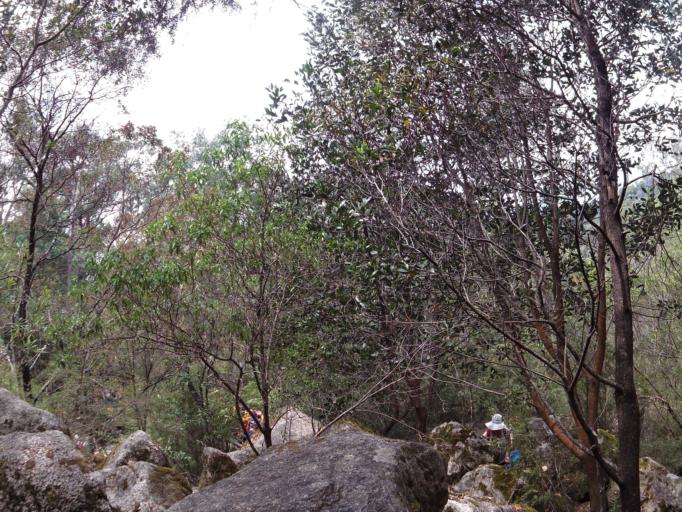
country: AU
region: Victoria
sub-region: Alpine
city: Mount Beauty
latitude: -36.7176
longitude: 146.8390
